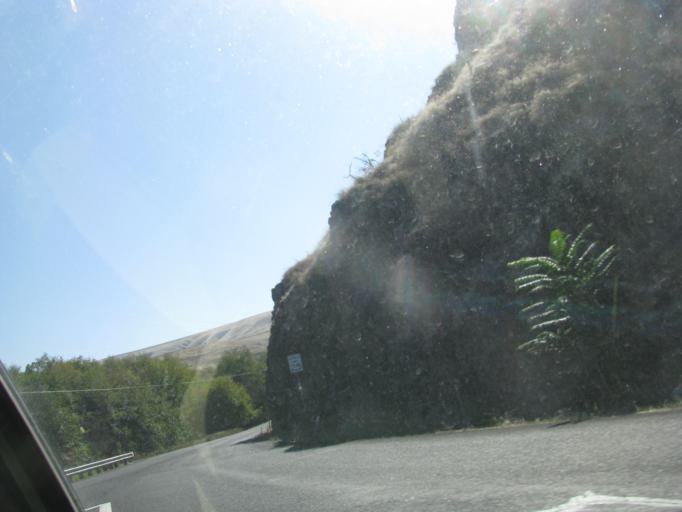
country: US
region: Washington
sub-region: Asotin County
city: Asotin
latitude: 46.3419
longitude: -117.0562
